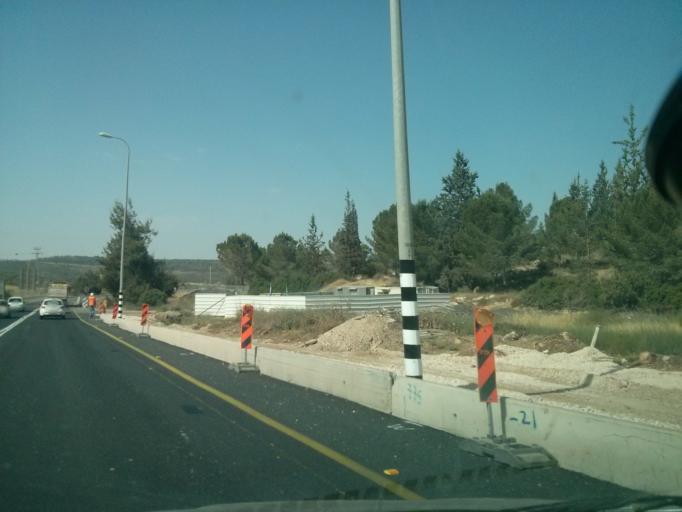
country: IL
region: Jerusalem
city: Bet Shemesh
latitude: 31.6950
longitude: 35.0107
